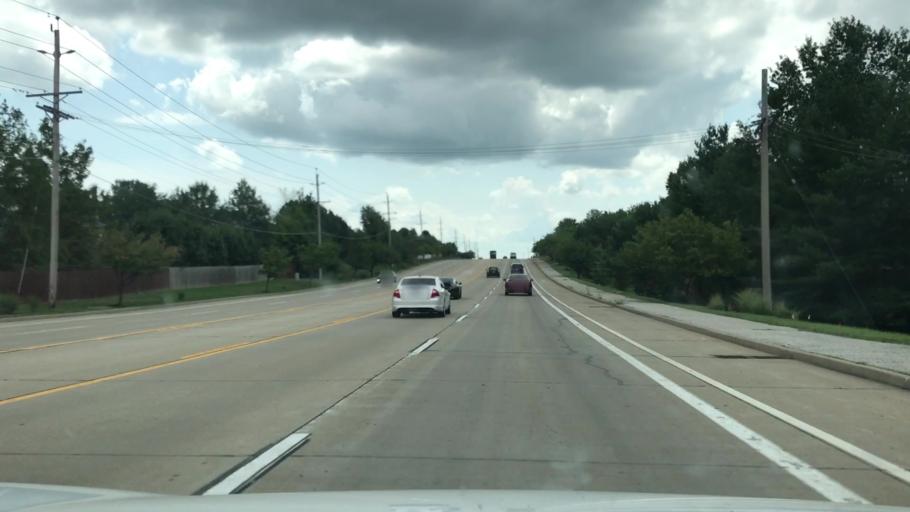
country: US
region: Missouri
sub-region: Saint Charles County
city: Weldon Spring
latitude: 38.7309
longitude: -90.6934
